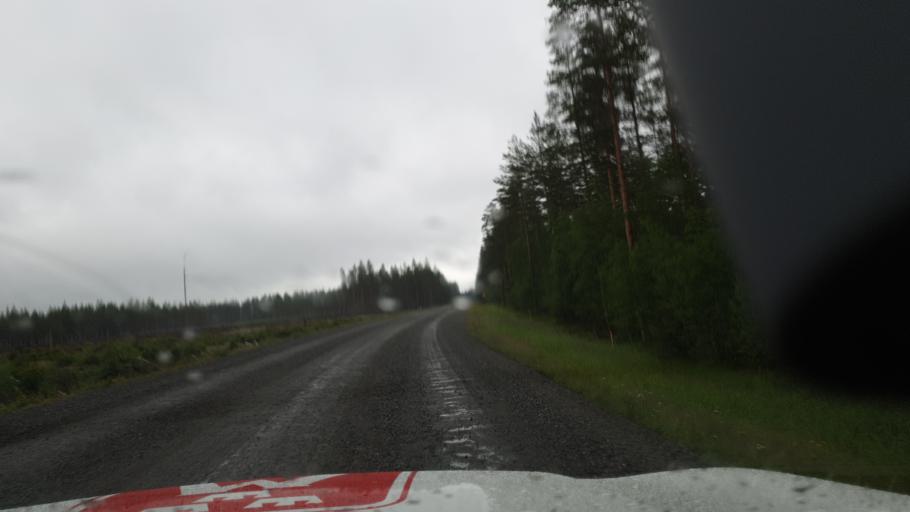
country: SE
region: Vaesterbotten
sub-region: Nordmalings Kommun
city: Nordmaling
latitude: 63.7018
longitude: 19.6220
